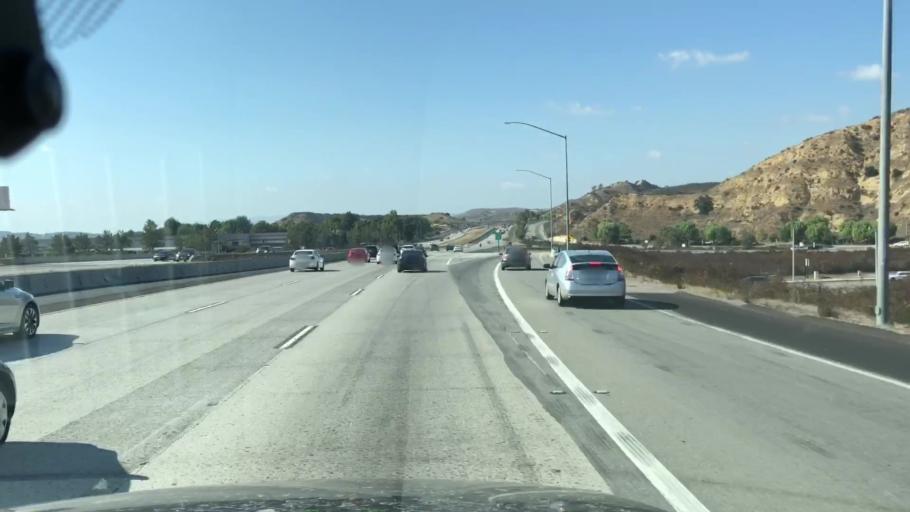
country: US
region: California
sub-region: Ventura County
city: Simi Valley
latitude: 34.2838
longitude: -118.7916
